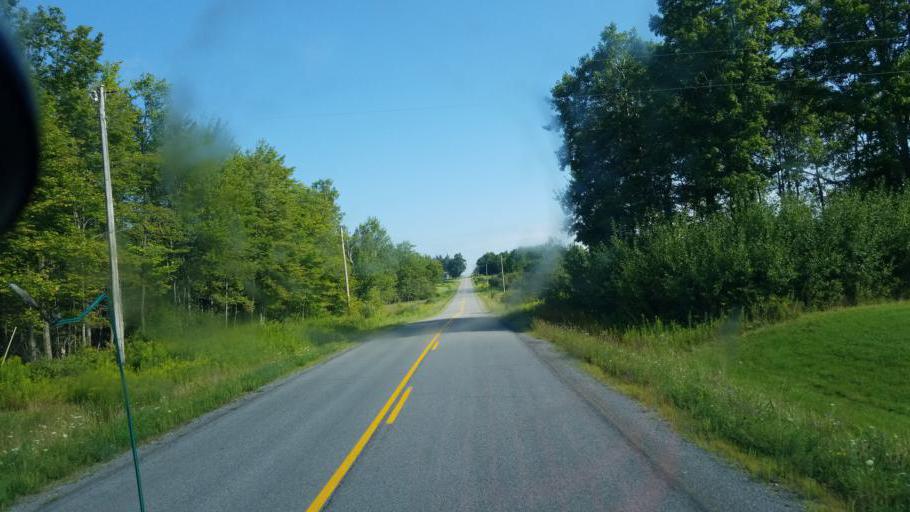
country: US
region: New York
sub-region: Allegany County
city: Andover
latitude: 42.1644
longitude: -77.7132
